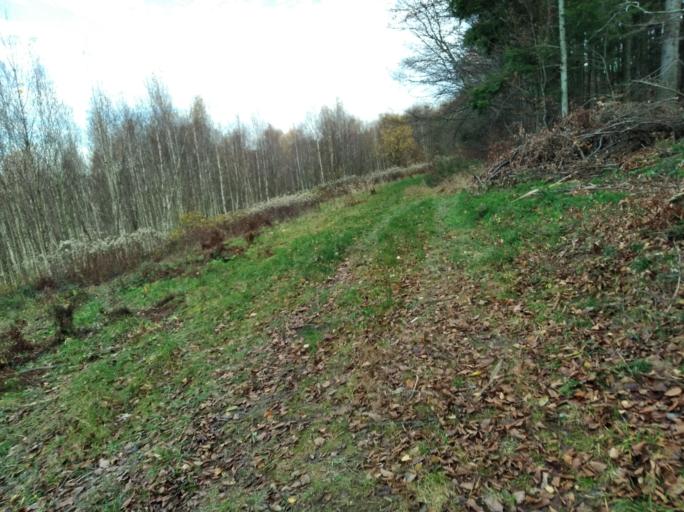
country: PL
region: Subcarpathian Voivodeship
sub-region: Powiat strzyzowski
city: Jawornik
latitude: 49.8548
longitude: 21.8492
